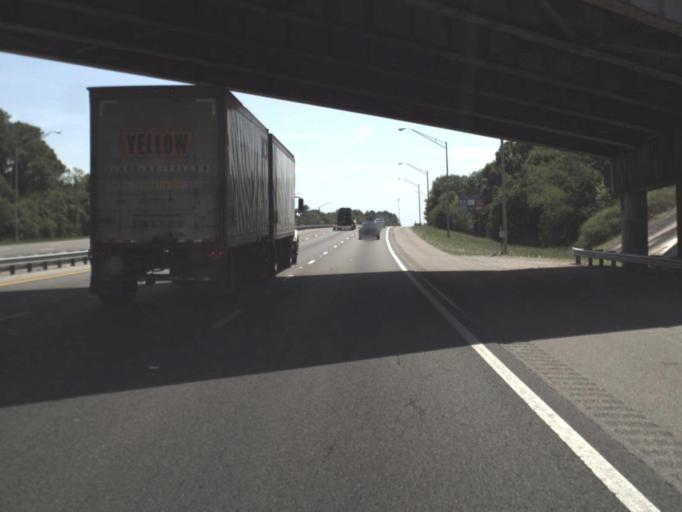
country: US
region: Florida
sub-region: Clay County
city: Bellair-Meadowbrook Terrace
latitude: 30.2581
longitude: -81.7635
